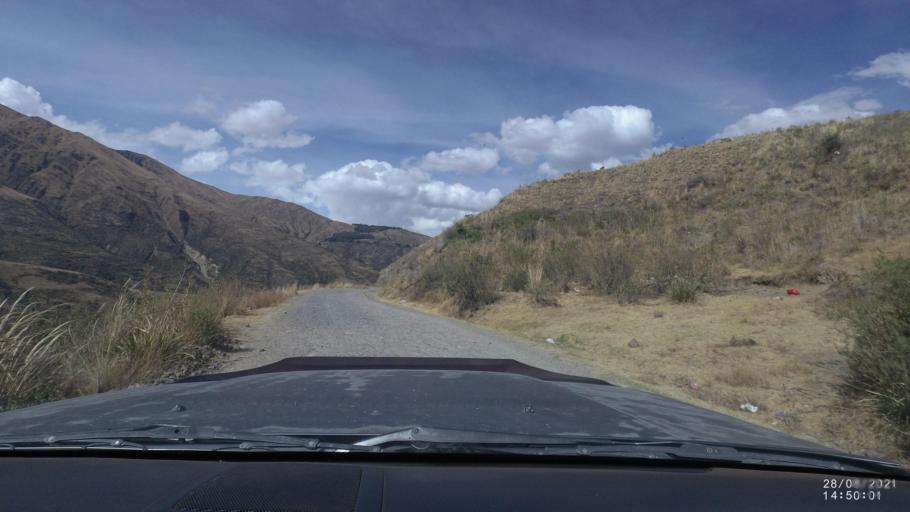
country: BO
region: Cochabamba
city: Sipe Sipe
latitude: -17.2842
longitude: -66.3126
